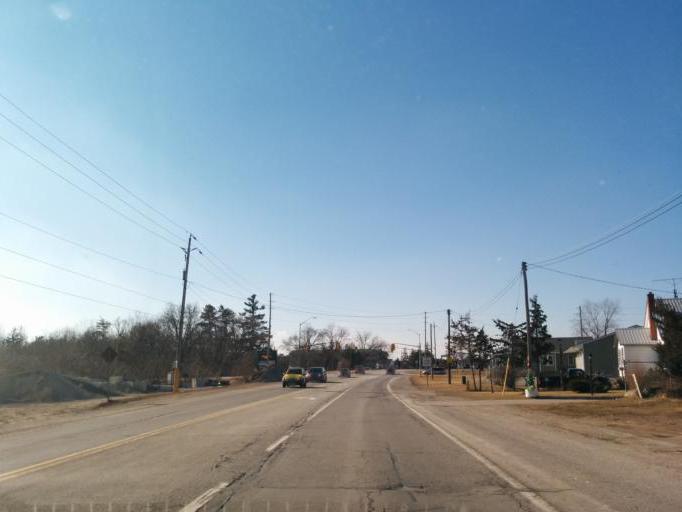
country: CA
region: Ontario
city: Norfolk County
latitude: 42.8423
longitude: -80.3253
